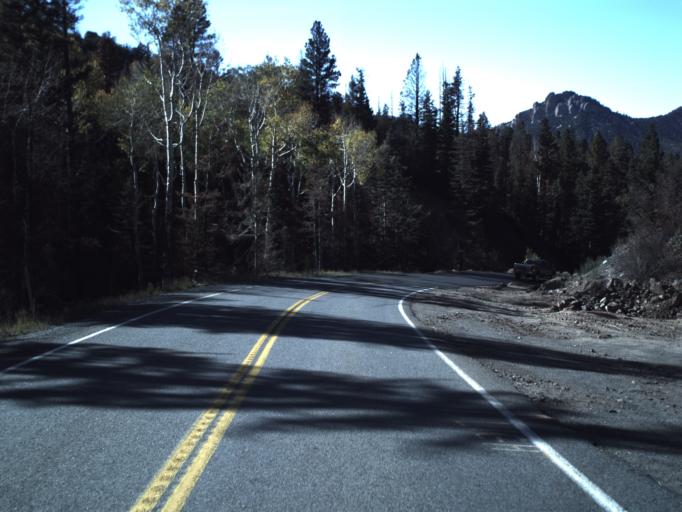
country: US
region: Utah
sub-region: Iron County
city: Parowan
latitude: 37.7525
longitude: -112.8385
